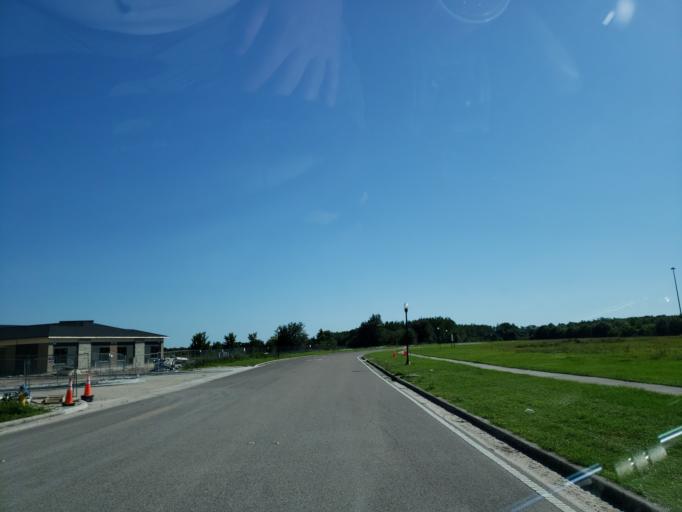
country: US
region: Florida
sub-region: Pasco County
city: Wesley Chapel
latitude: 28.2280
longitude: -82.3581
